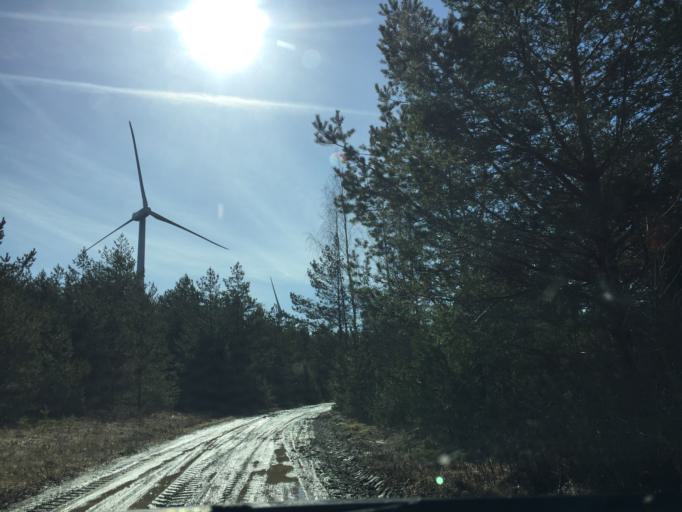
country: EE
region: Laeaene
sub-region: Haapsalu linn
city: Haapsalu
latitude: 58.6416
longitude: 23.5168
